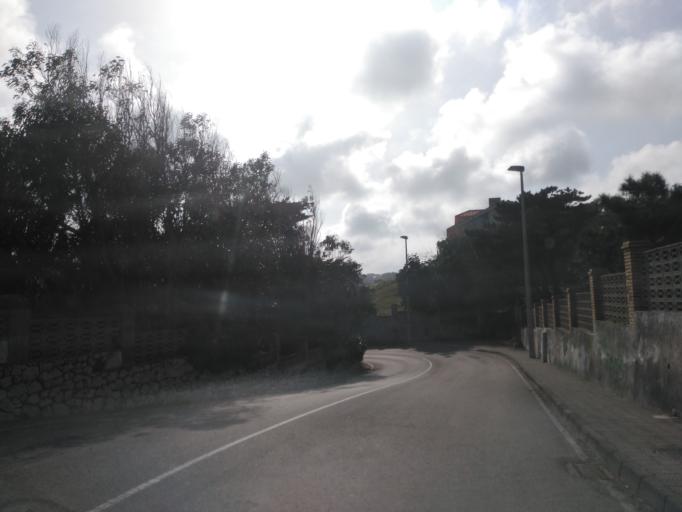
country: ES
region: Cantabria
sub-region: Provincia de Cantabria
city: Suances
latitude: 43.4361
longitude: -4.0460
